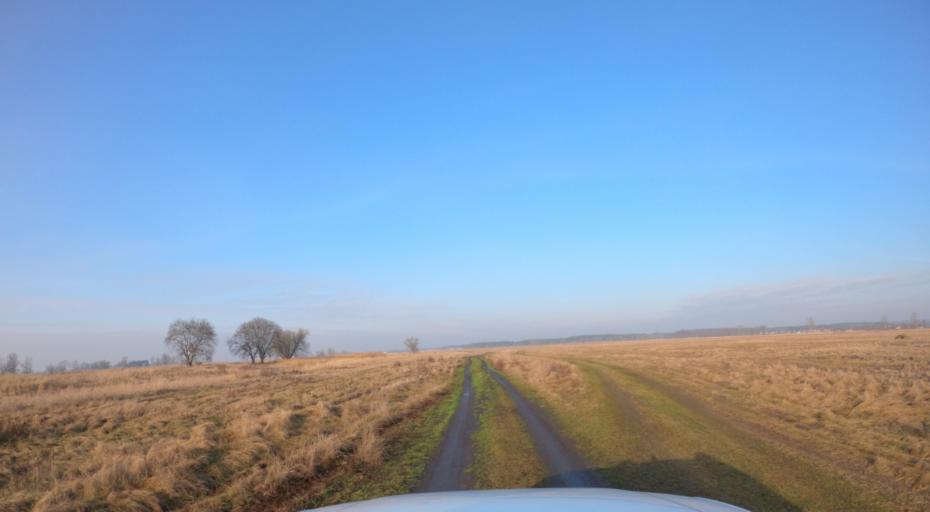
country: PL
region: Lubusz
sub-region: Powiat gorzowski
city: Kostrzyn nad Odra
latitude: 52.6053
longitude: 14.6062
